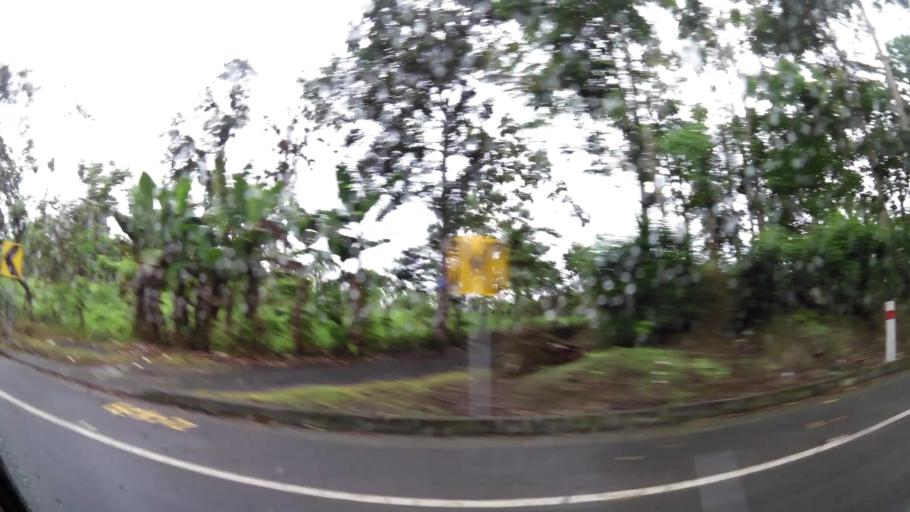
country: EC
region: Santo Domingo de los Tsachilas
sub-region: Canton Santo Domingo de los Colorados
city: Santo Domingo de los Colorados
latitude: -0.2340
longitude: -79.1369
